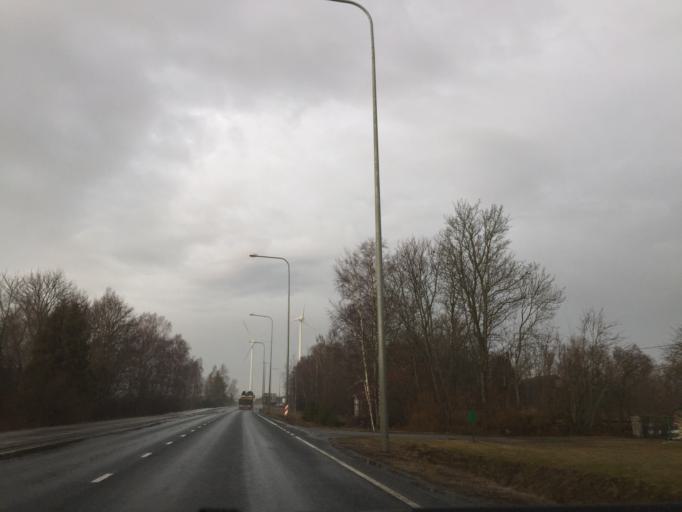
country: EE
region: Laeaene
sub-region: Lihula vald
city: Lihula
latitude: 58.5837
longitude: 23.5256
